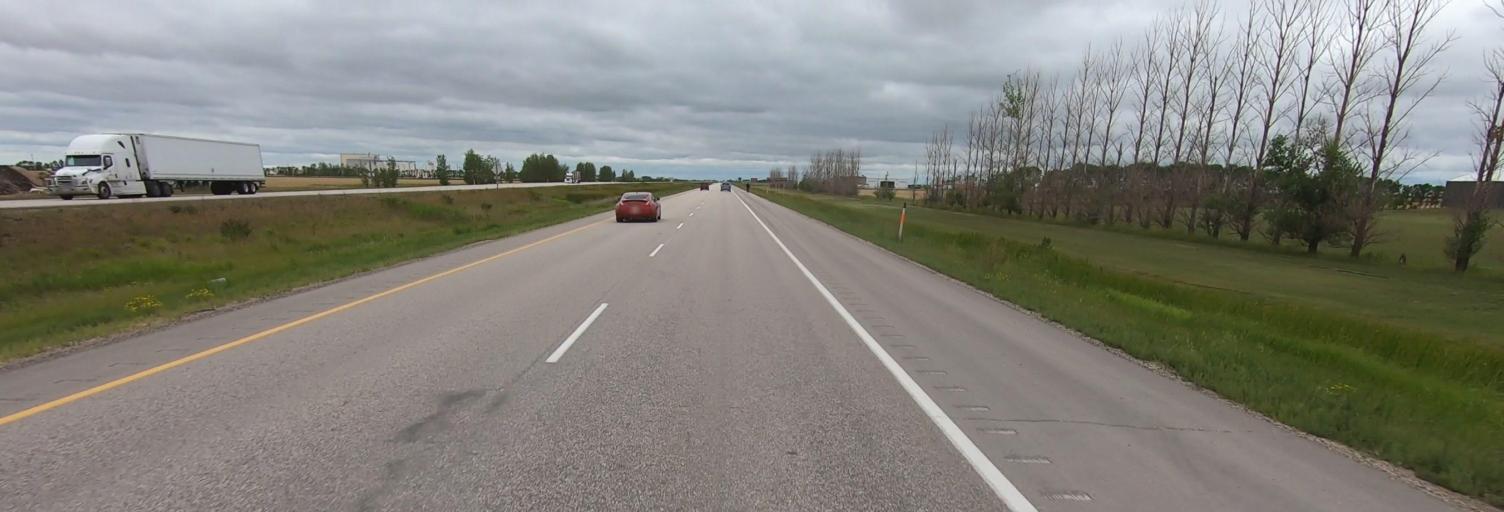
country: CA
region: Manitoba
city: Headingley
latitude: 49.9096
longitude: -97.7696
